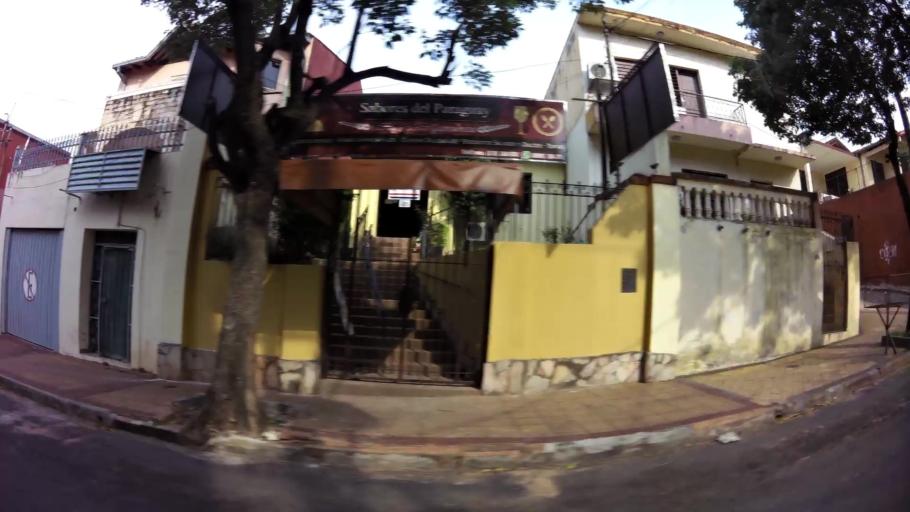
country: PY
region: Asuncion
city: Asuncion
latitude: -25.2962
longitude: -57.6200
